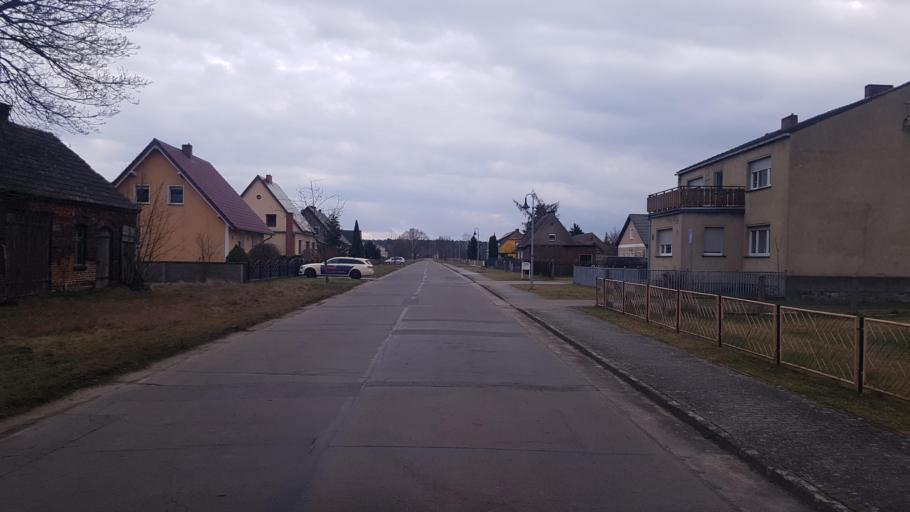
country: DE
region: Brandenburg
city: Drahnsdorf
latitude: 51.9230
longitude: 13.6413
